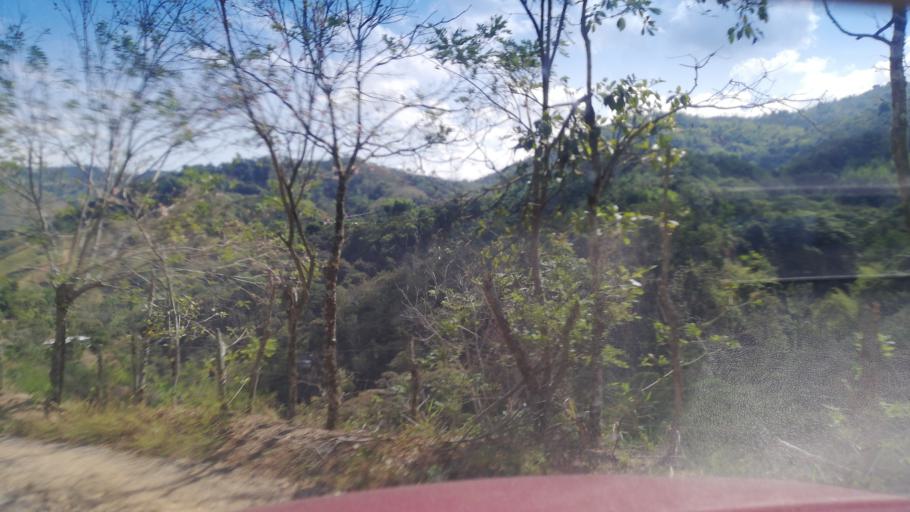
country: CO
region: Risaralda
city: Balboa
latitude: 4.9122
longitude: -75.9521
